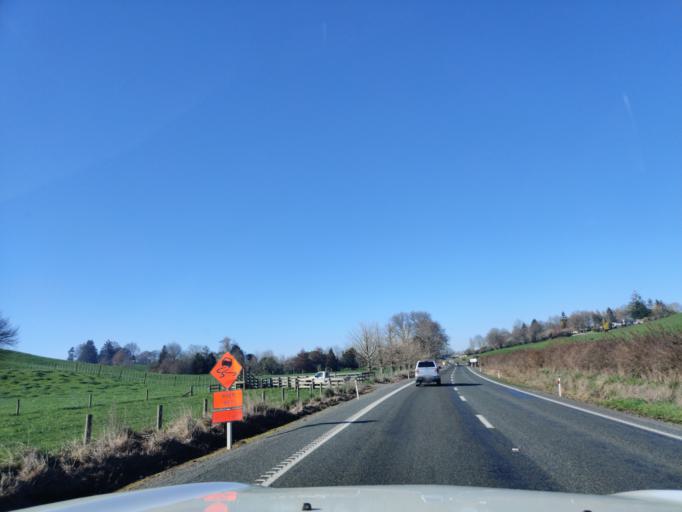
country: NZ
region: Waikato
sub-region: Matamata-Piako District
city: Matamata
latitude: -38.0081
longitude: 175.7715
